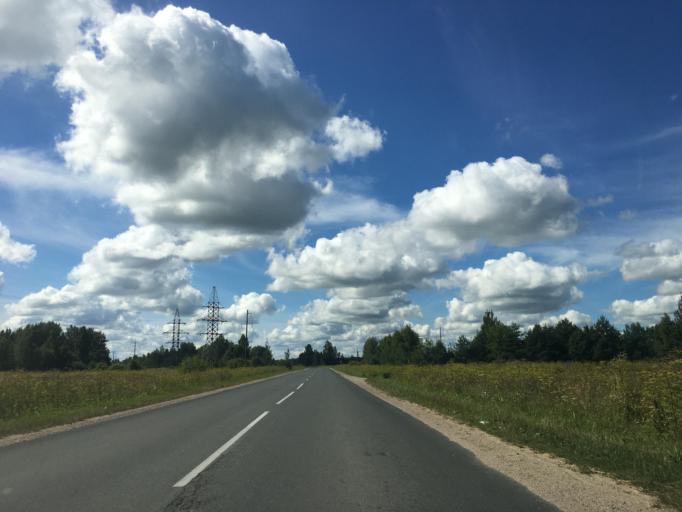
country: RU
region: Pskov
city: Pskov
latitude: 57.7767
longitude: 28.1656
